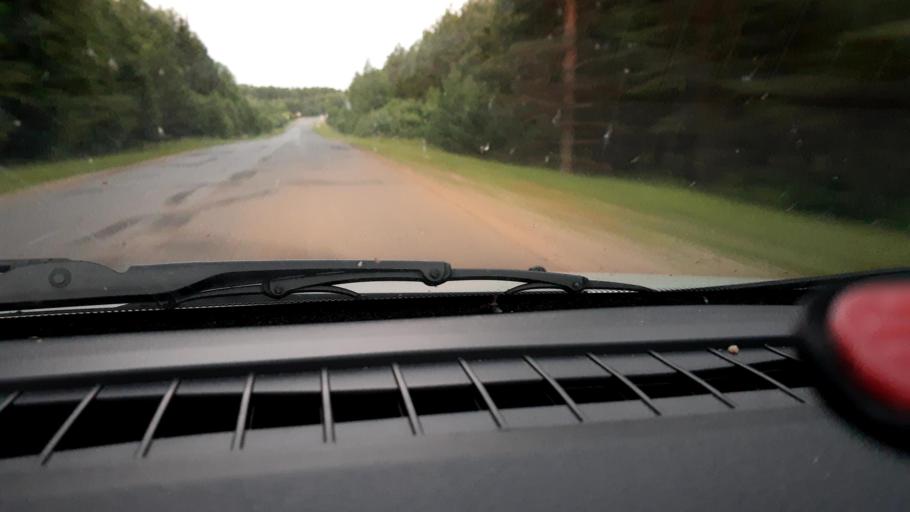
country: RU
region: Nizjnij Novgorod
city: Uren'
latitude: 57.4837
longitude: 46.0250
